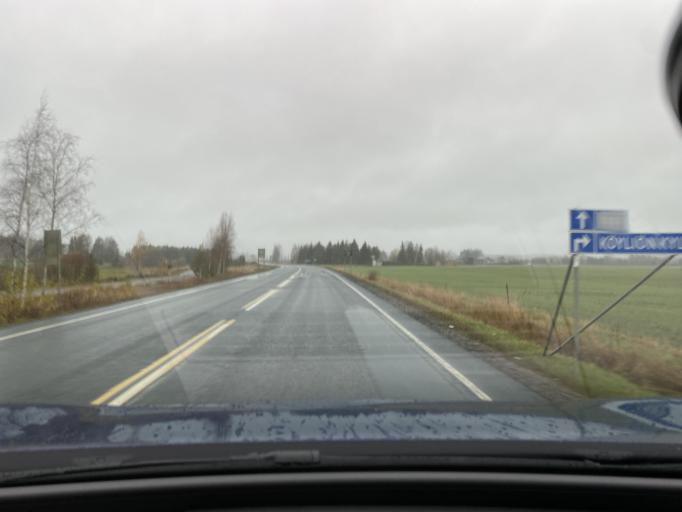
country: FI
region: Varsinais-Suomi
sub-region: Loimaa
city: Alastaro
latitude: 60.8889
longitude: 22.9699
